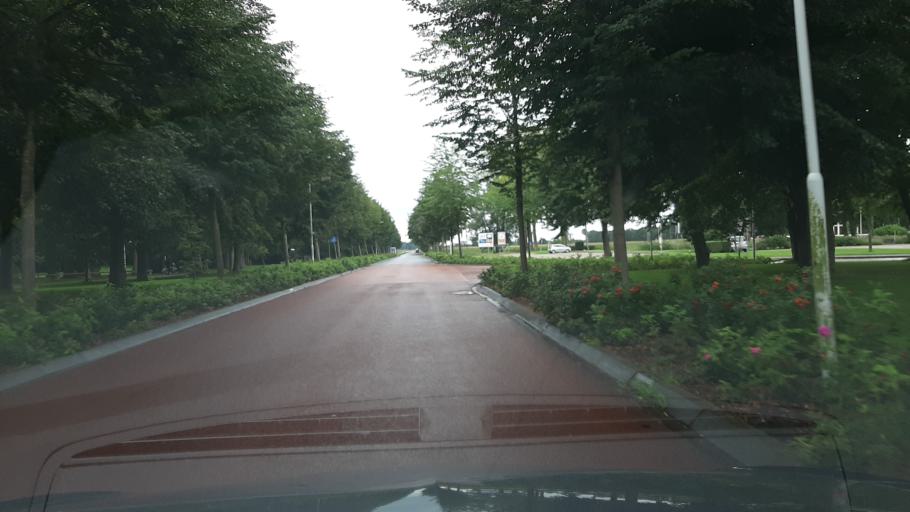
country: NL
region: Friesland
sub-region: Gemeente Weststellingwerf
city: Wolvega
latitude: 52.8716
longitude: 6.0072
